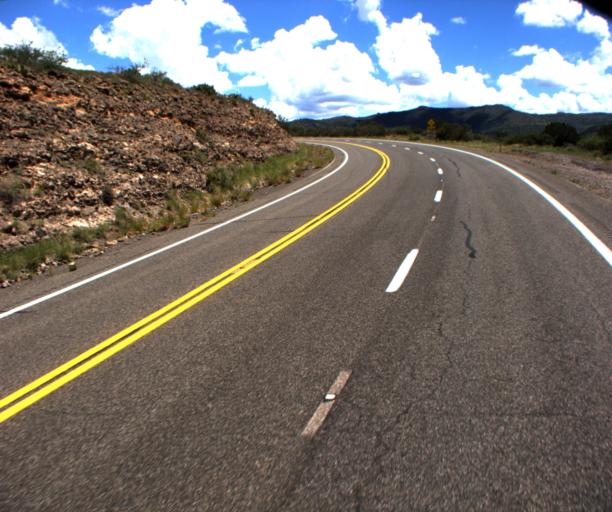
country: US
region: Arizona
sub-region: Yavapai County
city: Lake Montezuma
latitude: 34.4861
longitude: -111.7001
